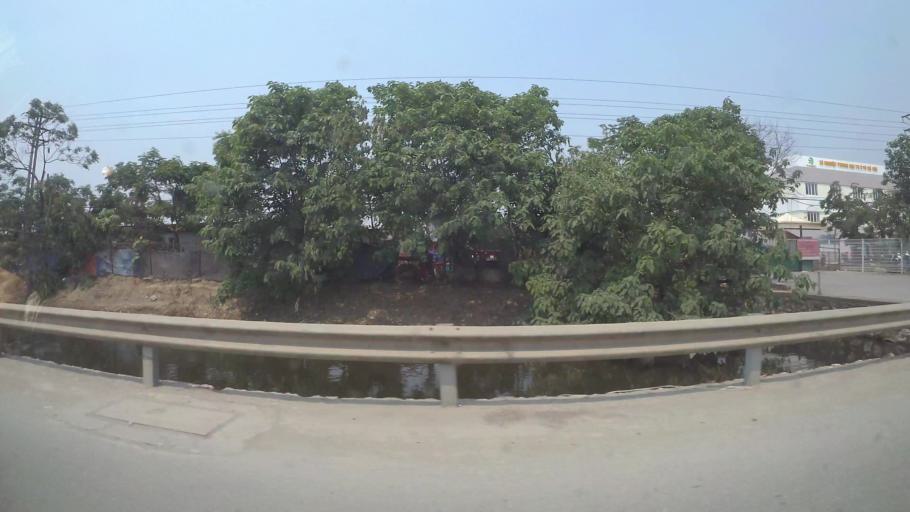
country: VN
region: Ha Noi
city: Van Dien
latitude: 20.9539
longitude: 105.8140
